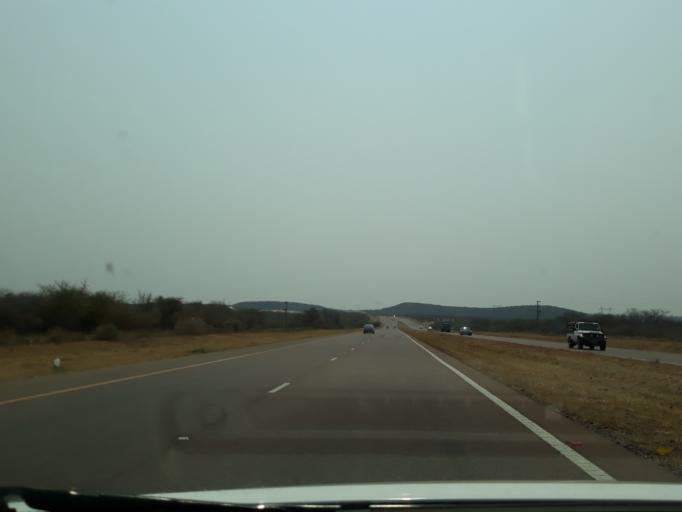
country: BW
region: Kgatleng
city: Bokaa
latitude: -24.4091
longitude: 26.0524
